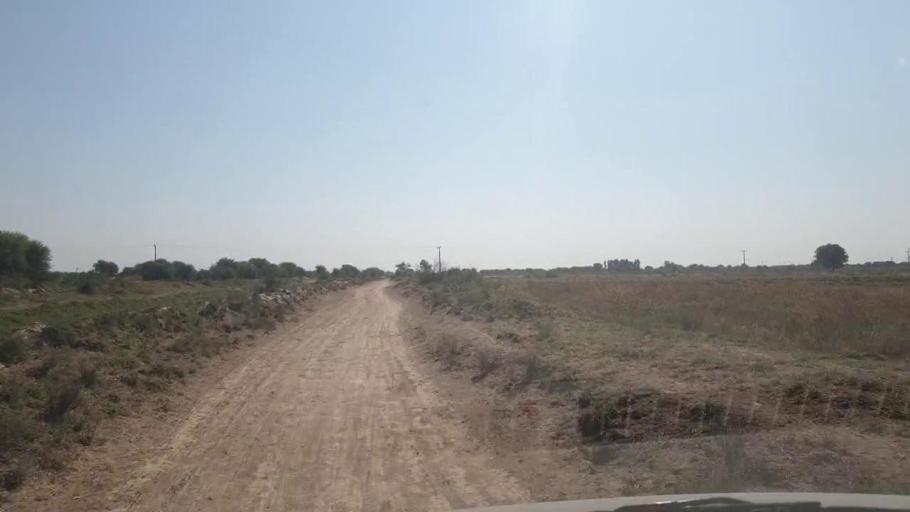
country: PK
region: Sindh
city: Digri
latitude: 24.9347
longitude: 69.1632
